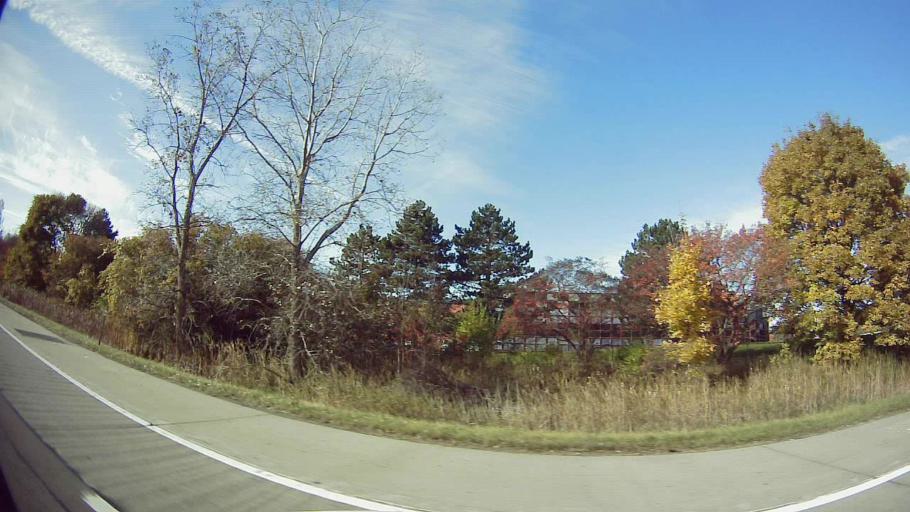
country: US
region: Michigan
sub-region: Wayne County
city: Westland
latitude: 42.3313
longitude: -83.4437
